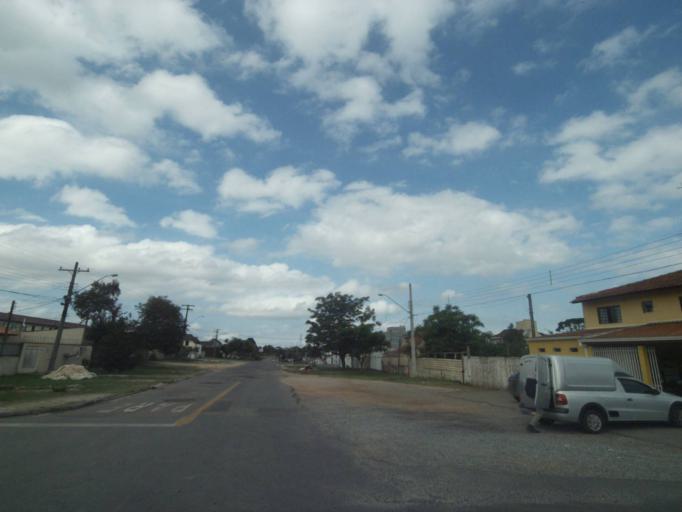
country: BR
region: Parana
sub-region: Pinhais
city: Pinhais
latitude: -25.4122
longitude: -49.2013
